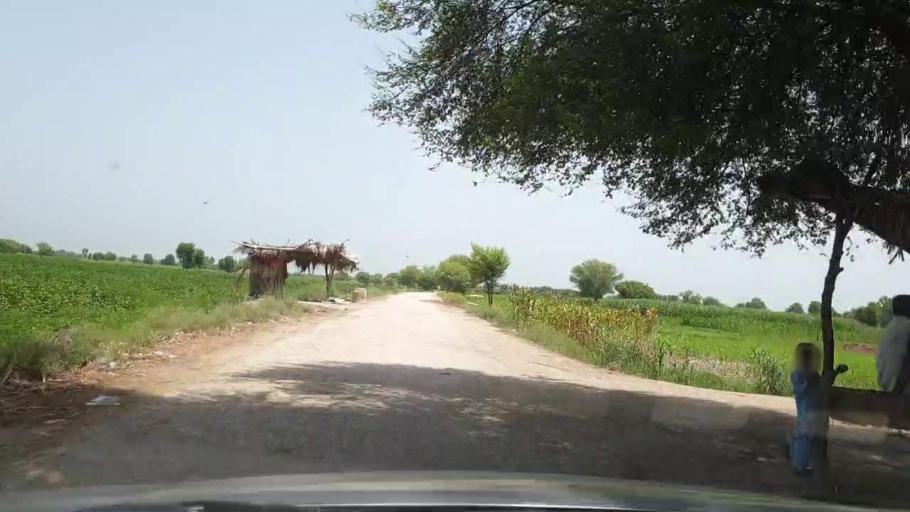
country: PK
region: Sindh
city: Pano Aqil
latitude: 27.8320
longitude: 69.1920
